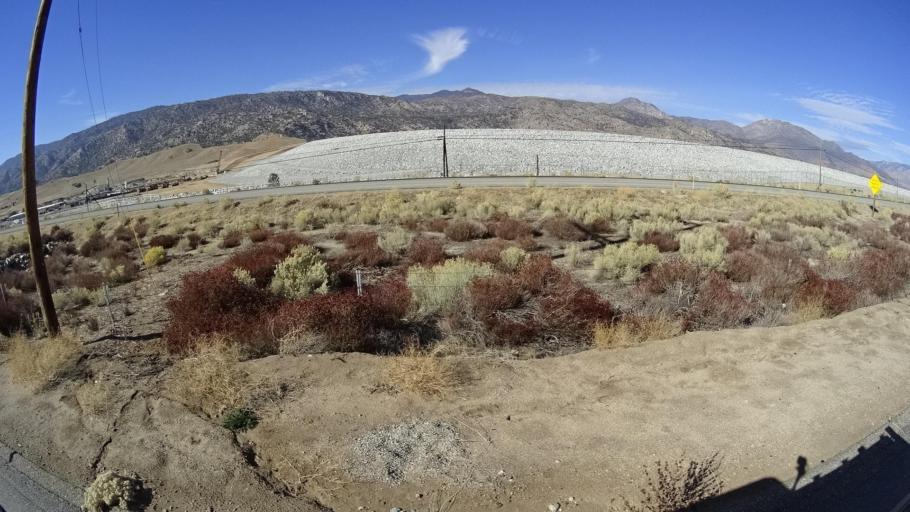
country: US
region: California
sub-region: Kern County
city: Lake Isabella
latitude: 35.6447
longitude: -118.4626
